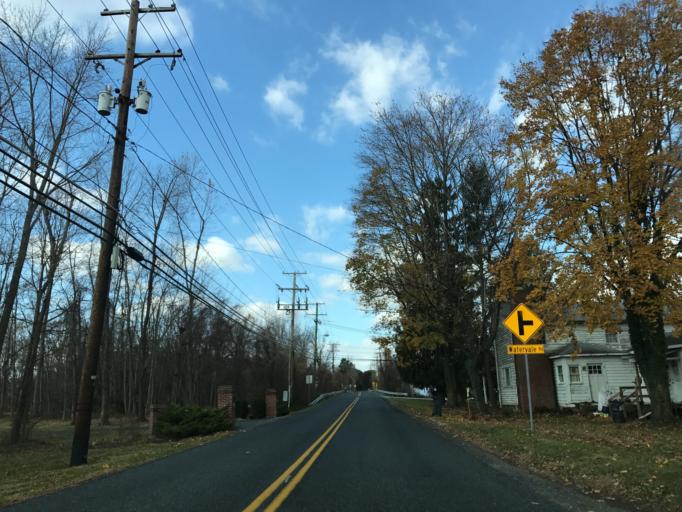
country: US
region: Maryland
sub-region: Harford County
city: Fallston
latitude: 39.5132
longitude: -76.4100
